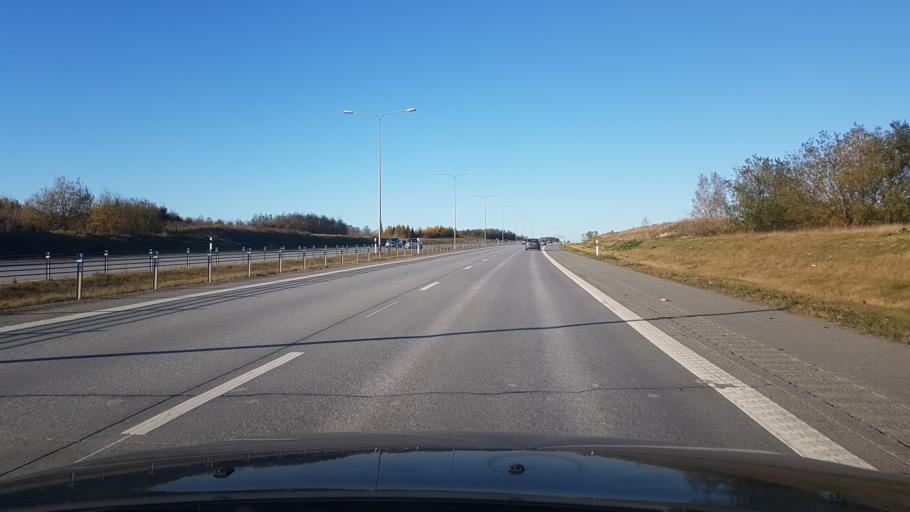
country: SE
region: Uppsala
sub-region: Uppsala Kommun
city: Saevja
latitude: 59.8680
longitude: 17.7091
